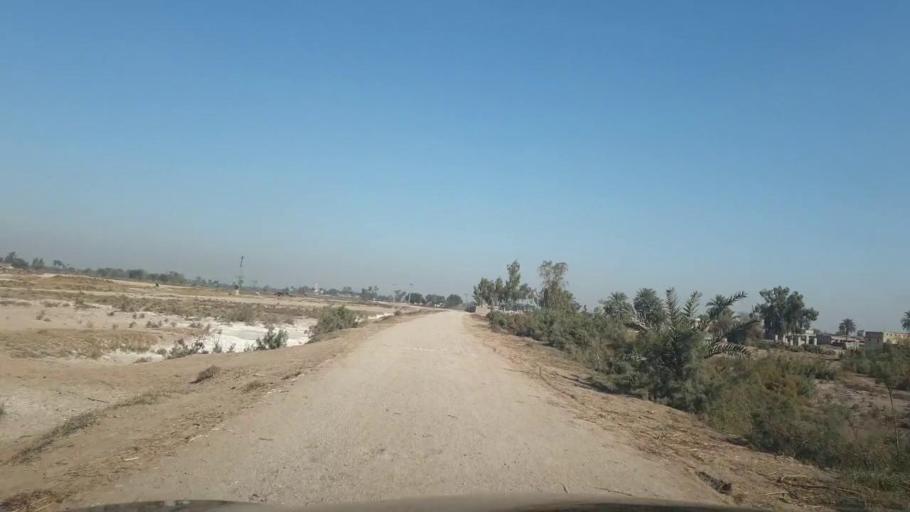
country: PK
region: Sindh
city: Ghotki
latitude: 27.9951
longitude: 69.3549
